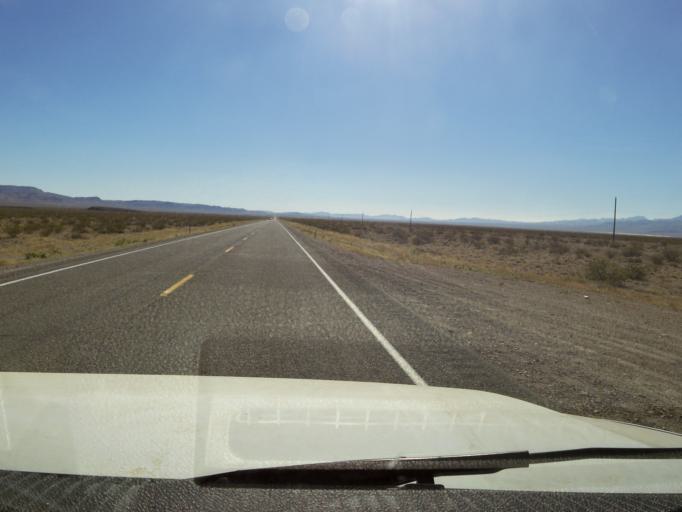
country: US
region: Nevada
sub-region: Esmeralda County
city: Goldfield
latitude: 37.3367
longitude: -117.0918
